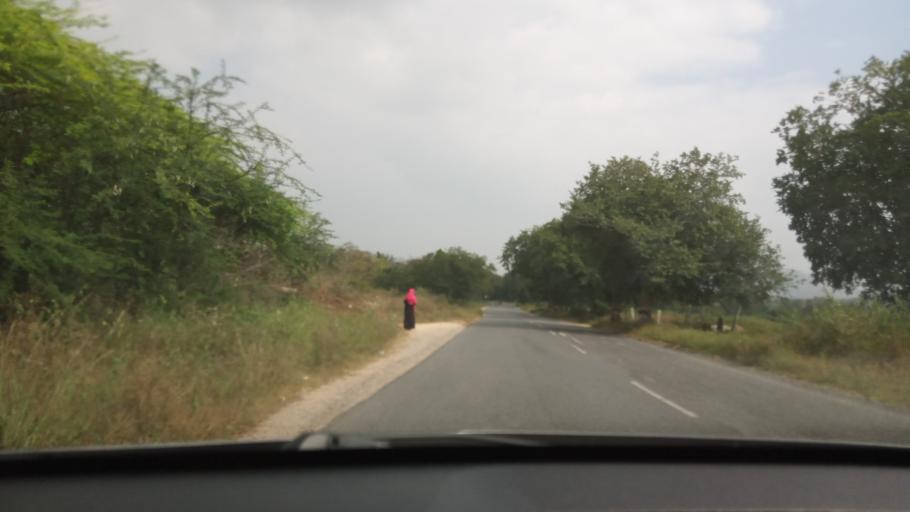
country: IN
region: Andhra Pradesh
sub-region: Chittoor
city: Madanapalle
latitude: 13.6520
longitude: 78.8268
